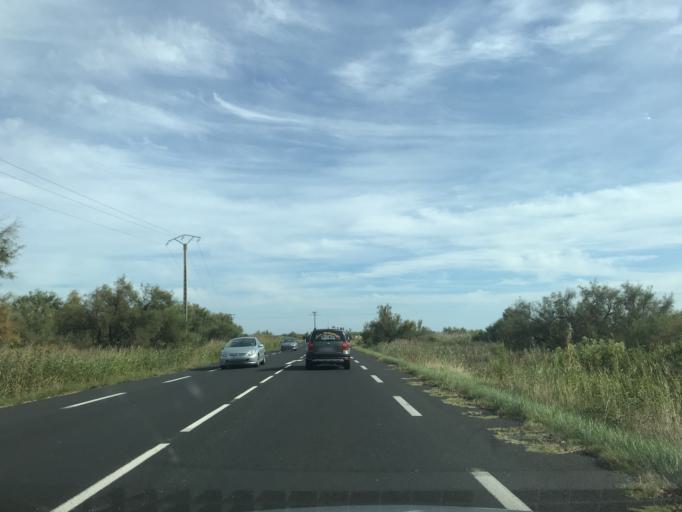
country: FR
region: Languedoc-Roussillon
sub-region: Departement du Gard
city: Aigues-Mortes
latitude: 43.5572
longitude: 4.3201
